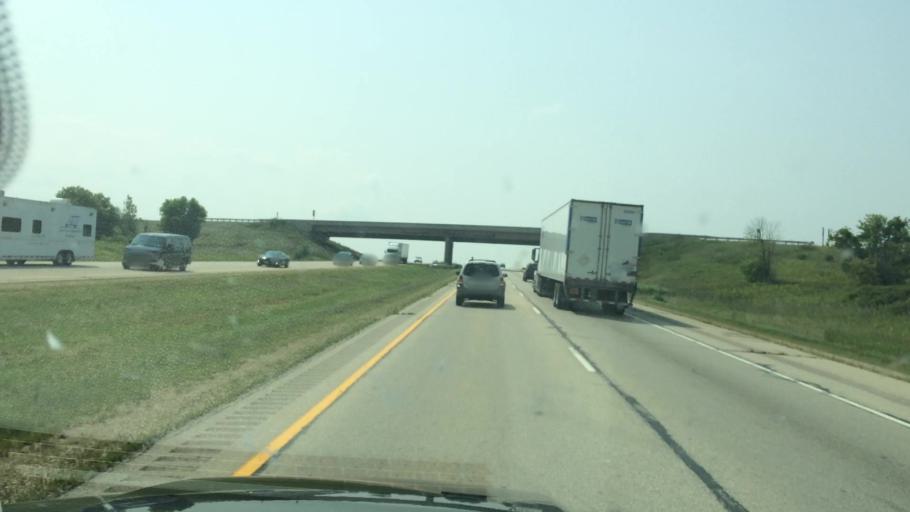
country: US
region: Wisconsin
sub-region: Dodge County
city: Theresa
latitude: 43.4744
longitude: -88.3669
